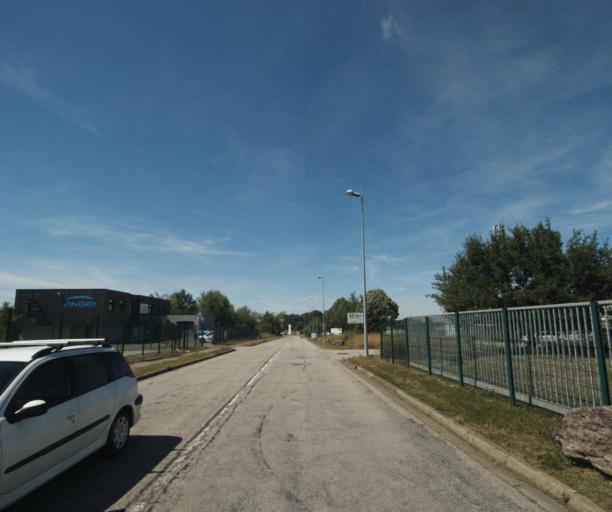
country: FR
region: Lorraine
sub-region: Departement des Vosges
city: Dogneville
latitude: 48.2024
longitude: 6.4612
